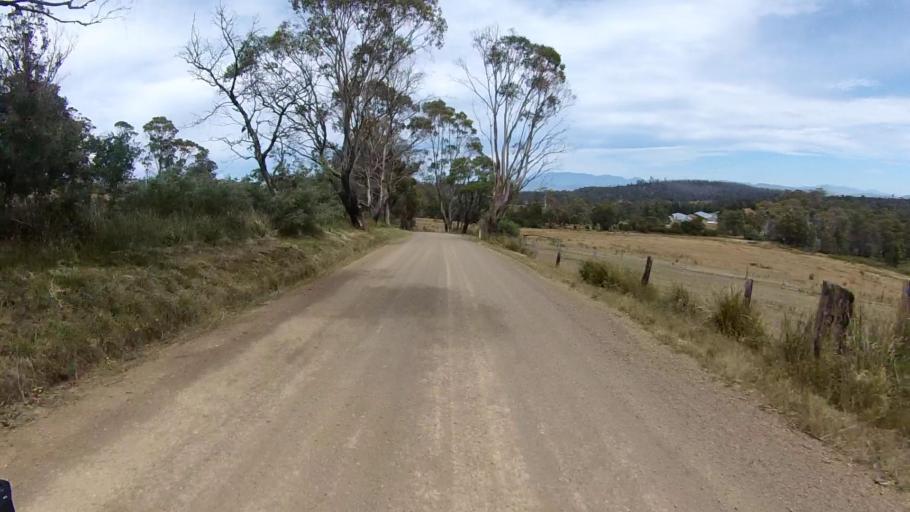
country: AU
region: Tasmania
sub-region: Sorell
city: Sorell
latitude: -42.7896
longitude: 147.6999
